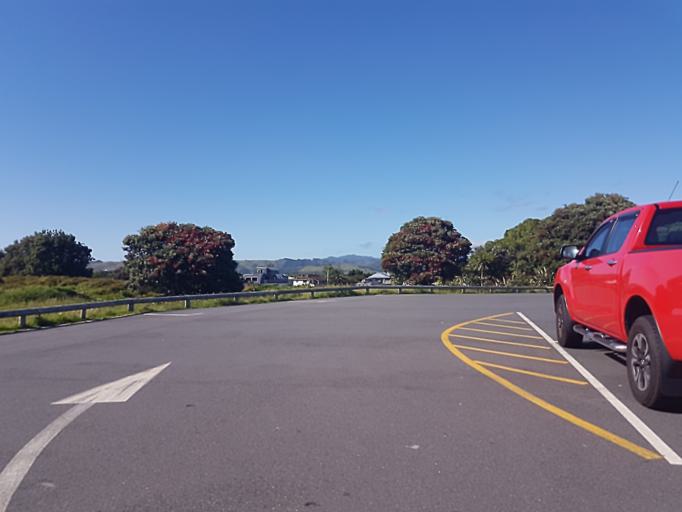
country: NZ
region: Bay of Plenty
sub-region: Tauranga City
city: Tauranga
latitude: -37.6940
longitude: 176.2805
